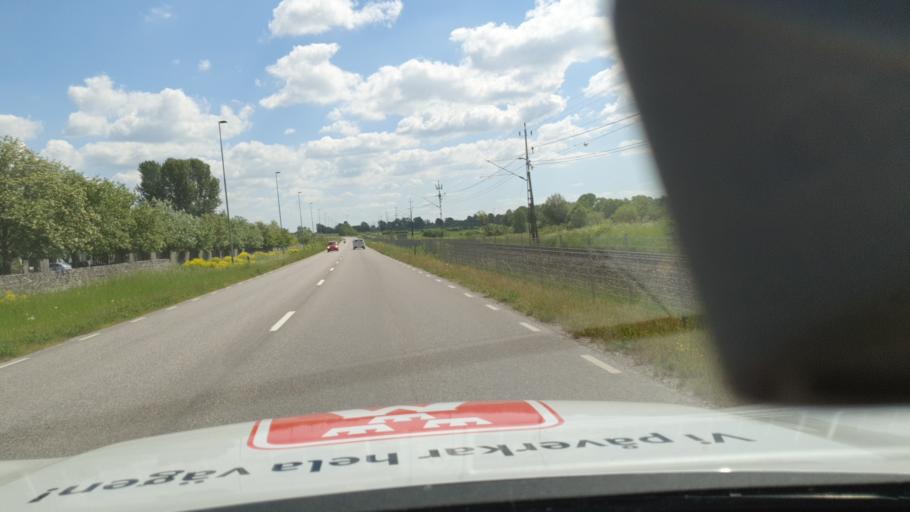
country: SE
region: Vaestra Goetaland
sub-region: Falkopings Kommun
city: Falkoeping
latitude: 58.1577
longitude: 13.5457
